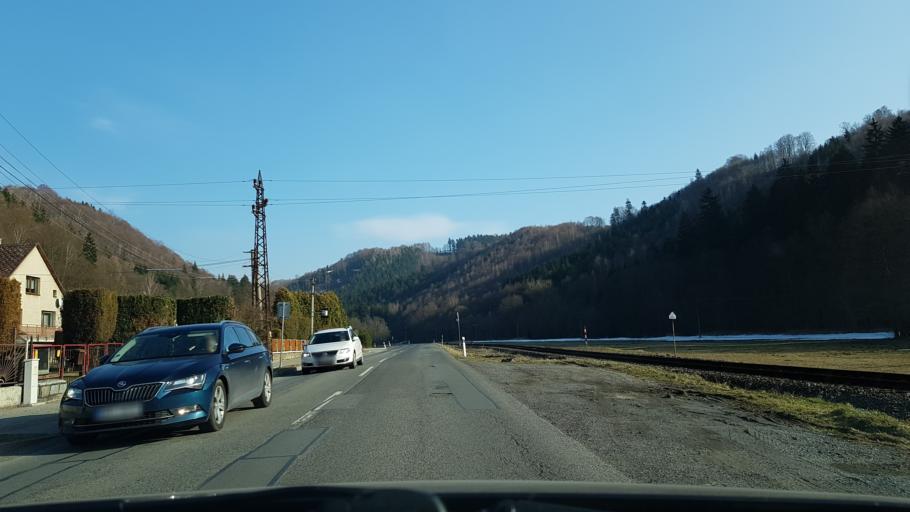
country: CZ
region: Olomoucky
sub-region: Okres Sumperk
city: Hanusovice
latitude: 50.0801
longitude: 16.9424
